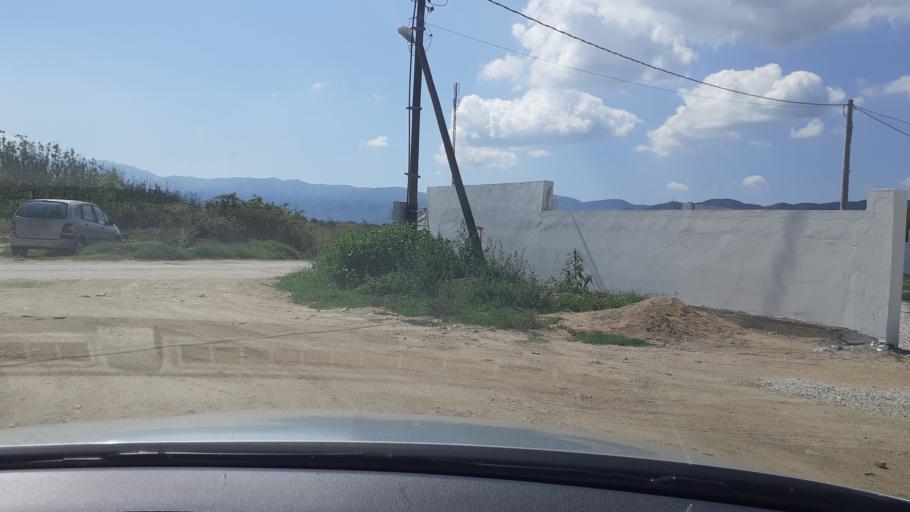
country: MK
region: Vasilevo
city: Vasilevo
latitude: 41.4677
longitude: 22.6426
